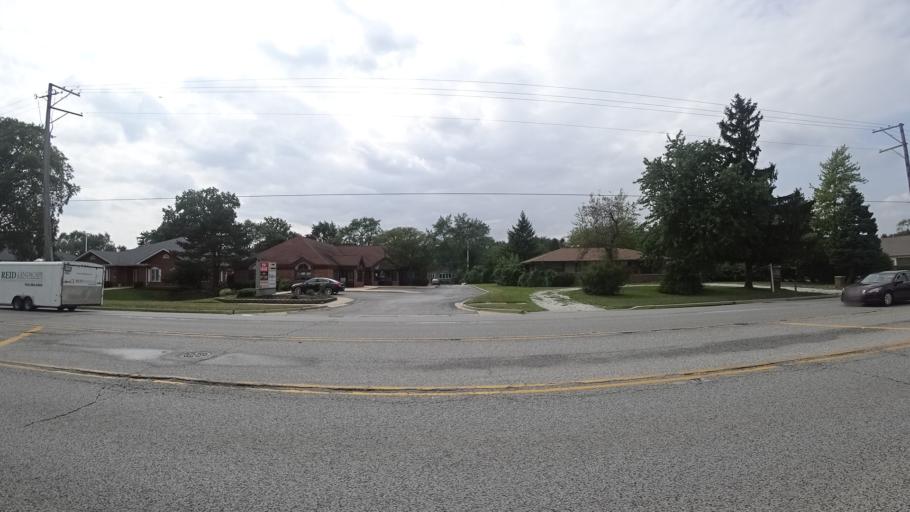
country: US
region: Illinois
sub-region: Cook County
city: Tinley Park
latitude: 41.5780
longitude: -87.7933
